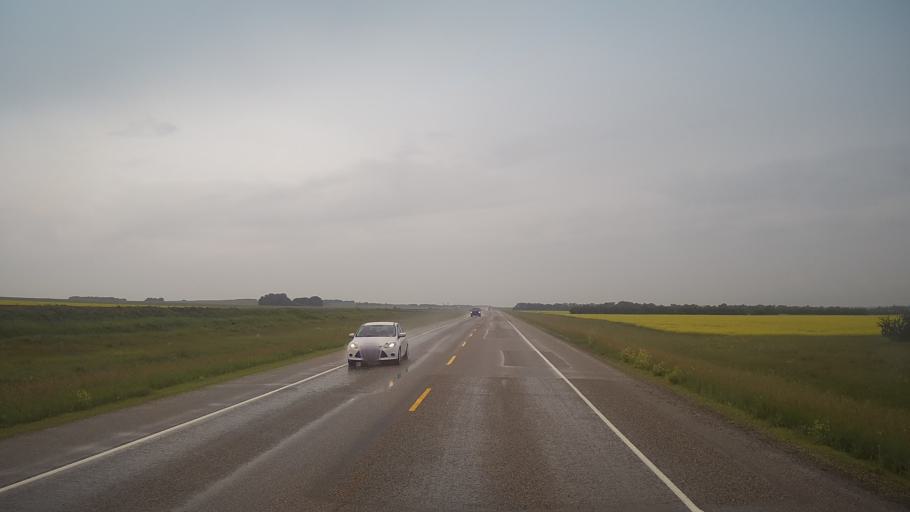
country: CA
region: Saskatchewan
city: Wilkie
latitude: 52.2330
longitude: -108.5461
